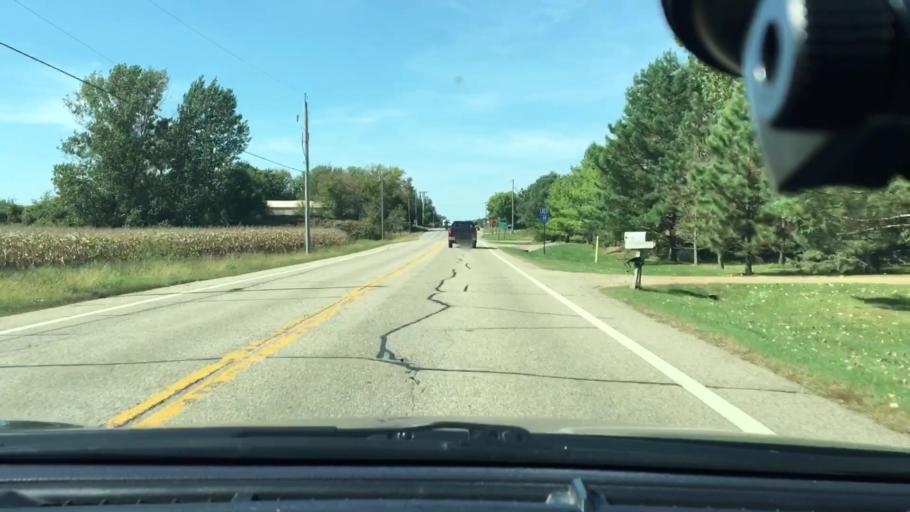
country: US
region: Minnesota
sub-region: Wright County
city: Hanover
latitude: 45.1237
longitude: -93.6308
